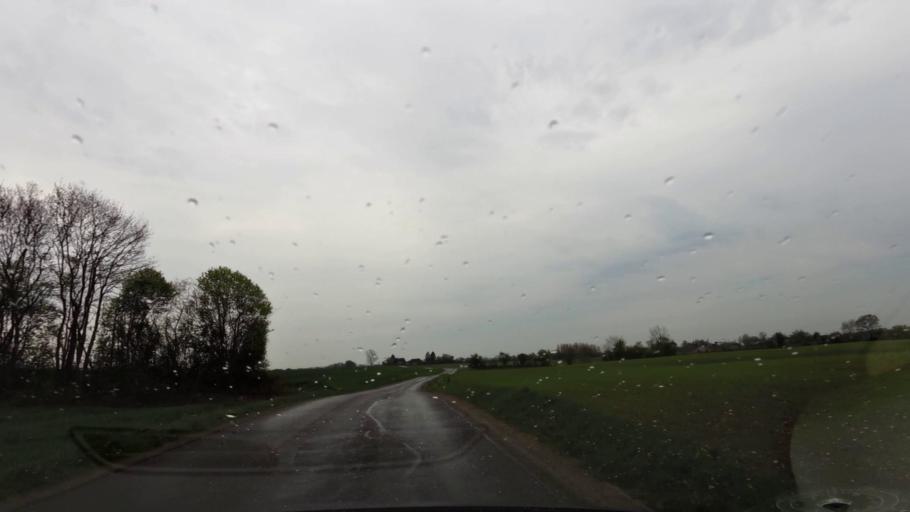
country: DK
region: South Denmark
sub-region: Svendborg Kommune
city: Svendborg
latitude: 55.1738
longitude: 10.5955
